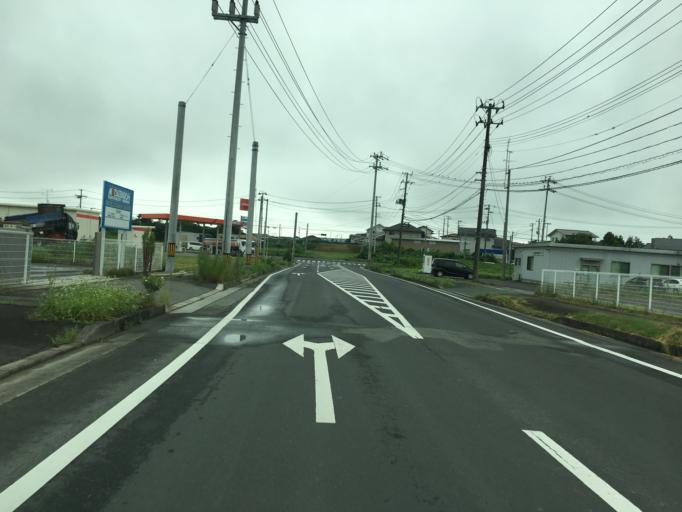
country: JP
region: Miyagi
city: Marumori
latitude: 37.8267
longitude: 140.9492
